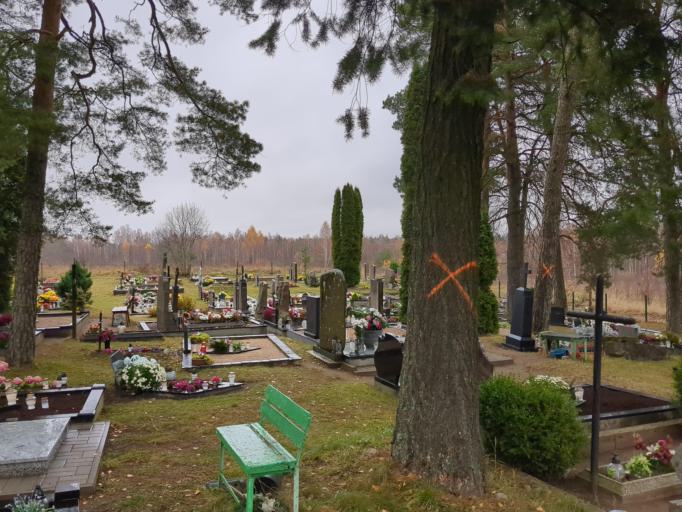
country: LT
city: Trakai
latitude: 54.6338
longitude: 24.9908
